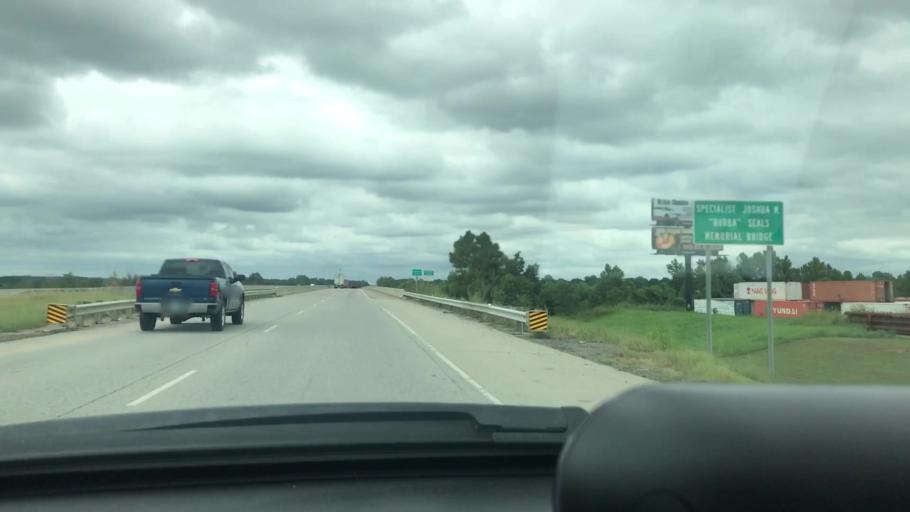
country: US
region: Oklahoma
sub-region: Muskogee County
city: Muskogee
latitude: 35.8033
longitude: -95.4017
